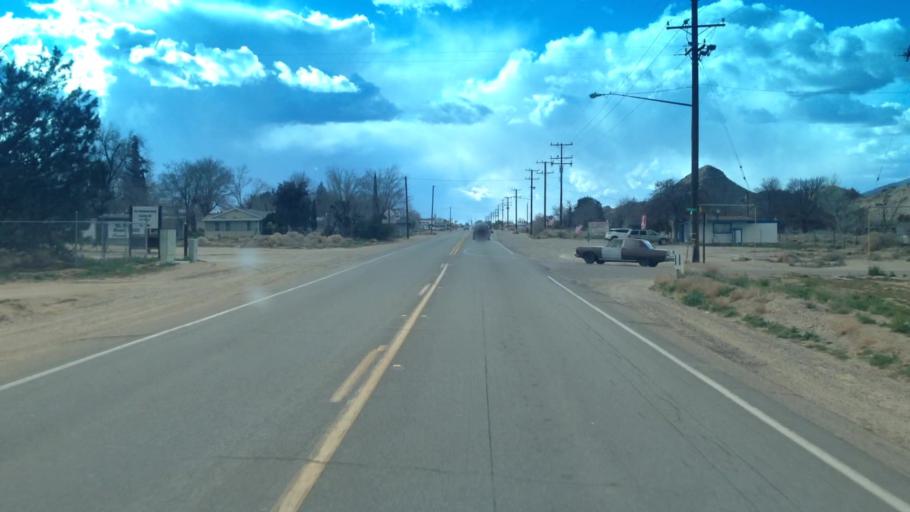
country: US
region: California
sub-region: San Bernardino County
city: Lucerne Valley
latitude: 34.4437
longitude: -116.9672
